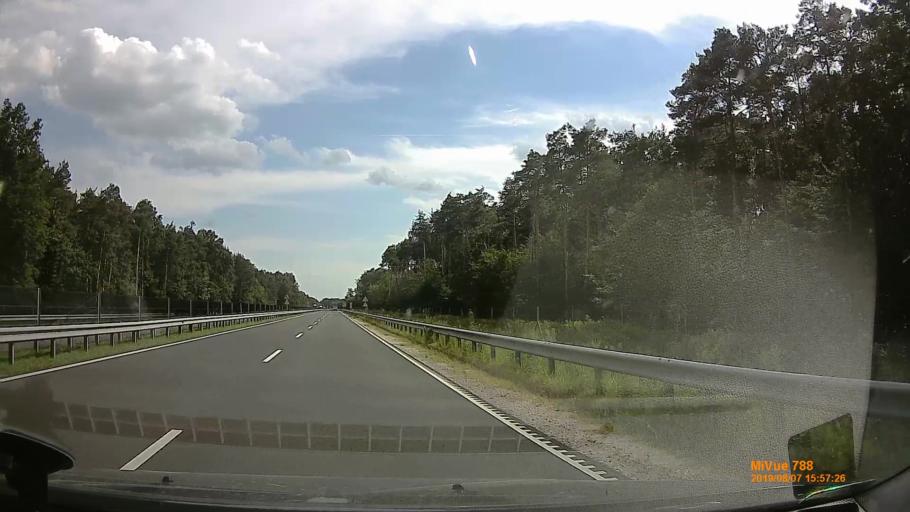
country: HU
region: Vas
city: Kormend
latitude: 47.0422
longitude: 16.6137
